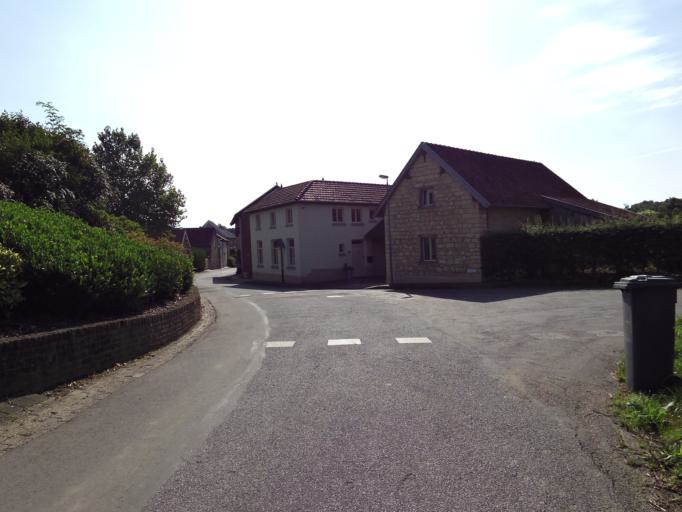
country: NL
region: Limburg
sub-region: Gemeente Voerendaal
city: Klimmen
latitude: 50.8634
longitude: 5.8857
